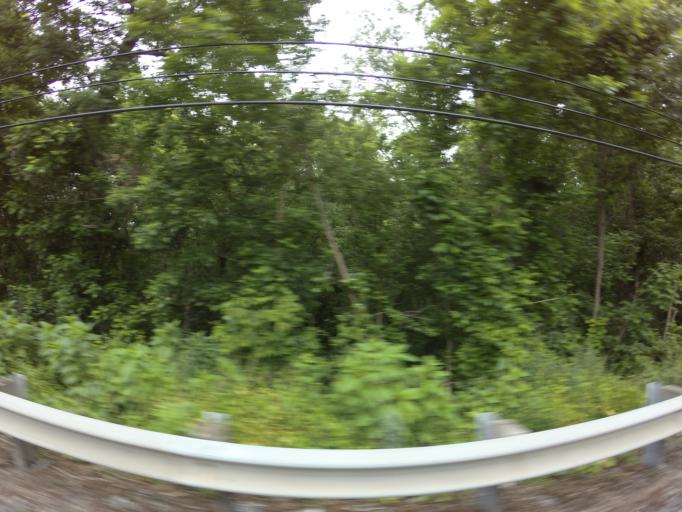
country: US
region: Maryland
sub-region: Frederick County
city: Jefferson
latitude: 39.3311
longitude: -77.5569
